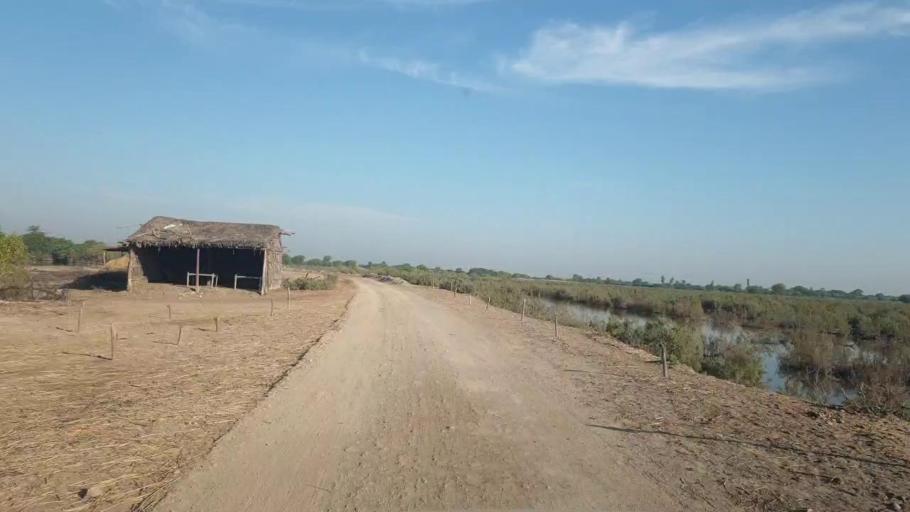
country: PK
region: Sindh
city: Talhar
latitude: 24.8177
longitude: 68.8398
